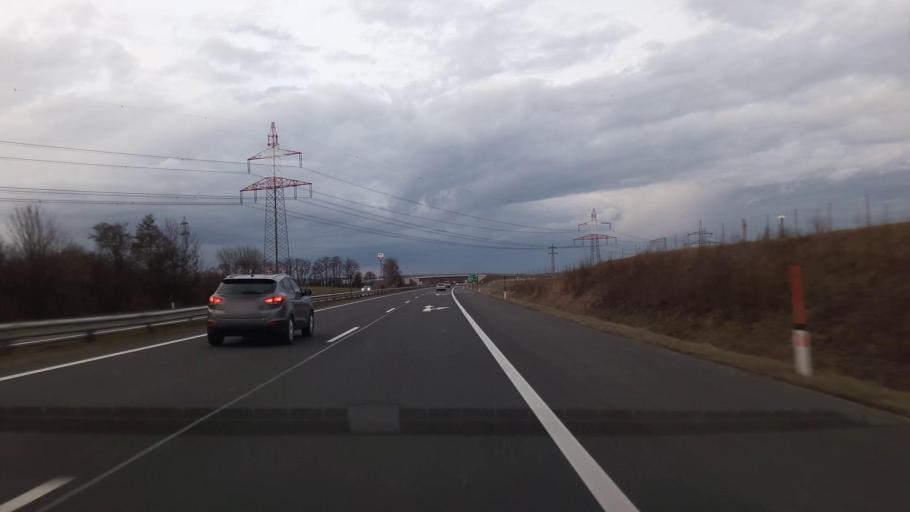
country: AT
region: Burgenland
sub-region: Eisenstadt-Umgebung
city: Hornstein
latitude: 47.8729
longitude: 16.4170
